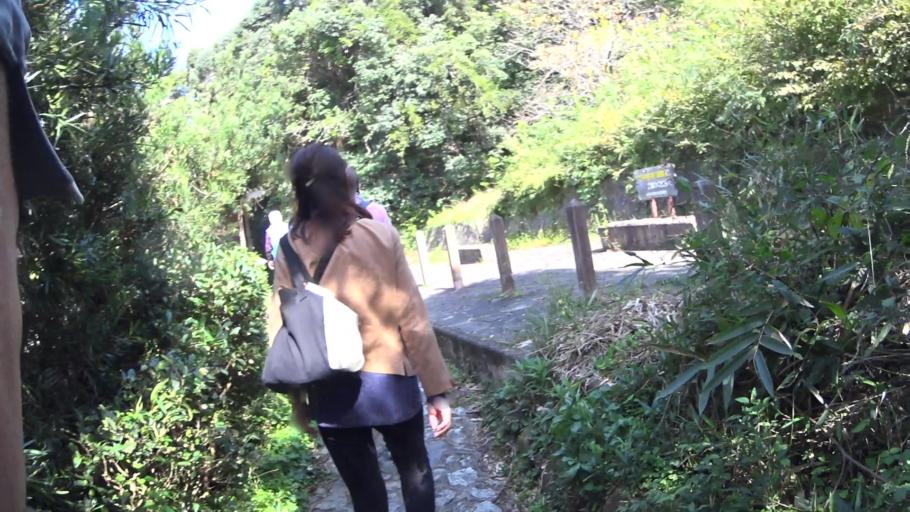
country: JP
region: Nara
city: Sakurai
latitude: 34.5319
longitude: 135.8517
